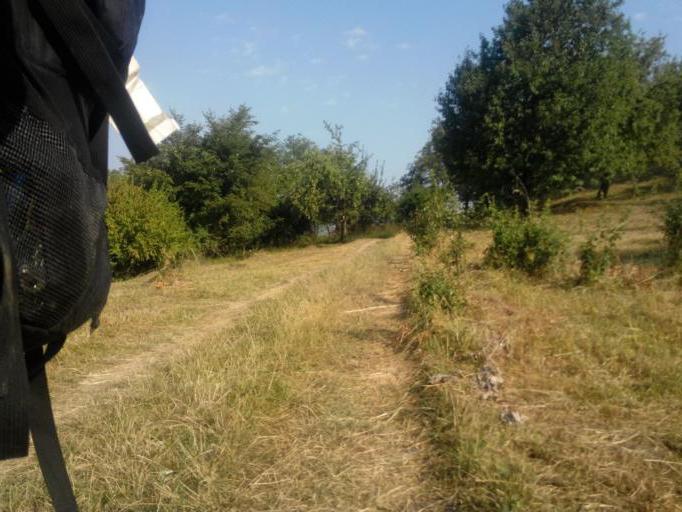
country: RO
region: Suceava
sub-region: Comuna Radaseni
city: Radaseni
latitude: 47.4626
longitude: 26.2616
